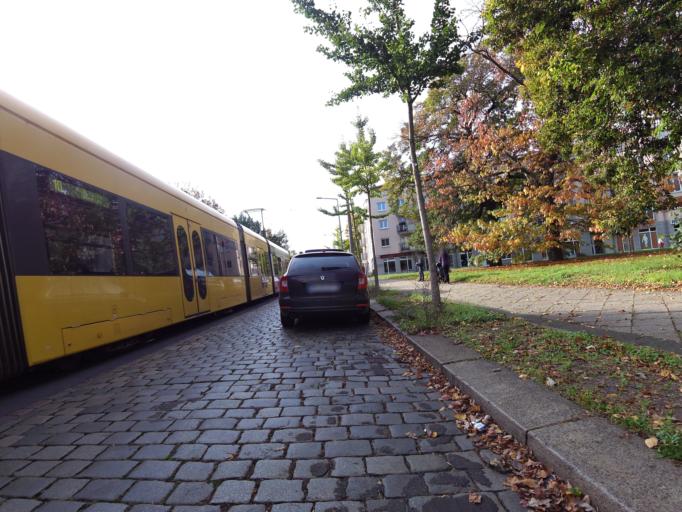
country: DE
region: Saxony
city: Dresden
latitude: 51.0470
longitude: 13.7650
